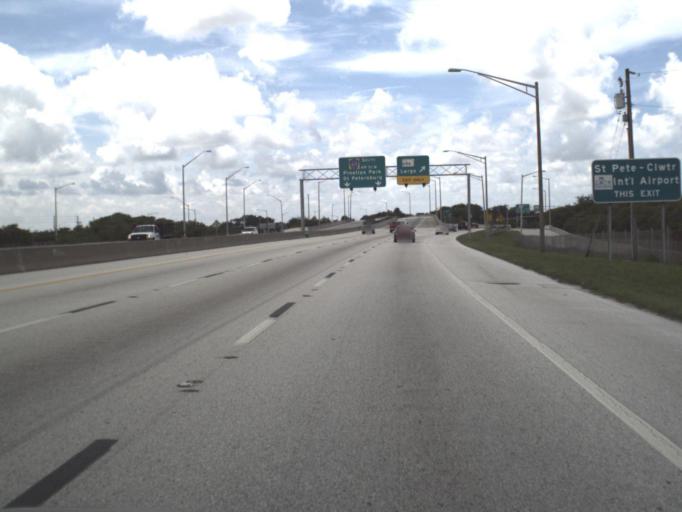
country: US
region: Florida
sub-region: Pinellas County
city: South Highpoint
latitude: 27.9142
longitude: -82.7005
